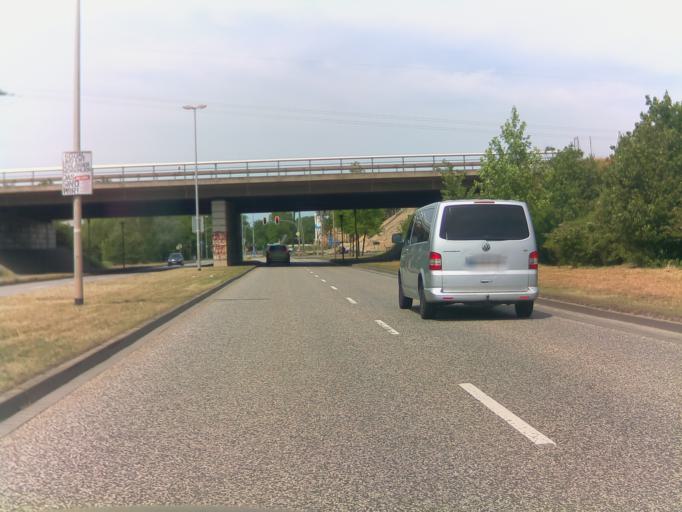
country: DE
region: Saxony-Anhalt
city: Glindenberg
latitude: 52.2110
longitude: 11.6669
